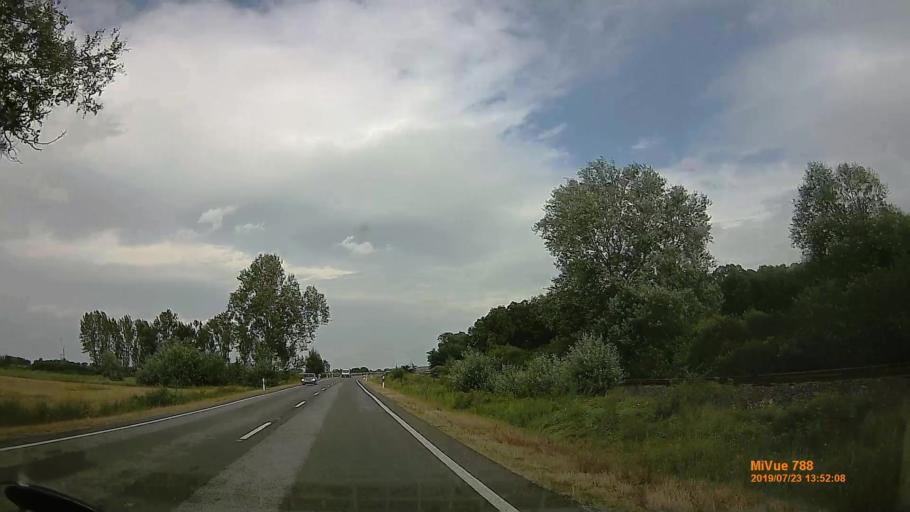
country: HU
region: Hajdu-Bihar
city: Polgar
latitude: 47.8985
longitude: 21.1569
